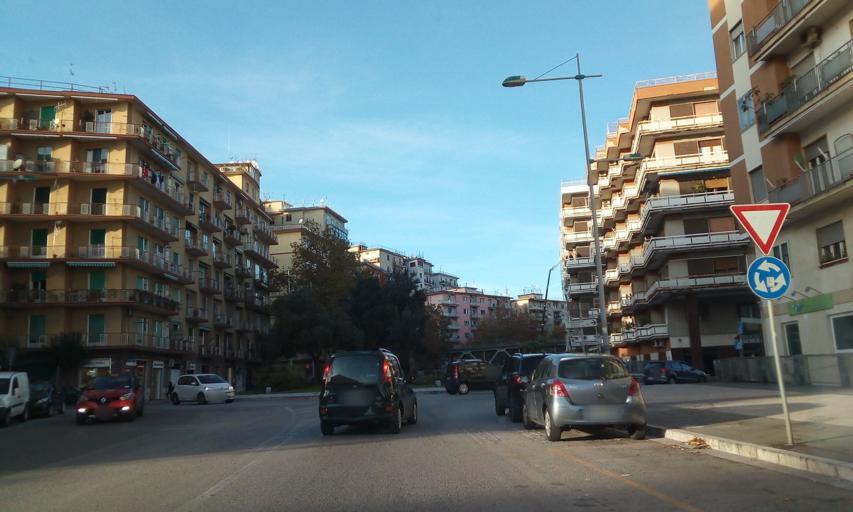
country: IT
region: Campania
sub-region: Provincia di Salerno
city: Salerno
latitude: 40.6809
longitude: 14.7743
